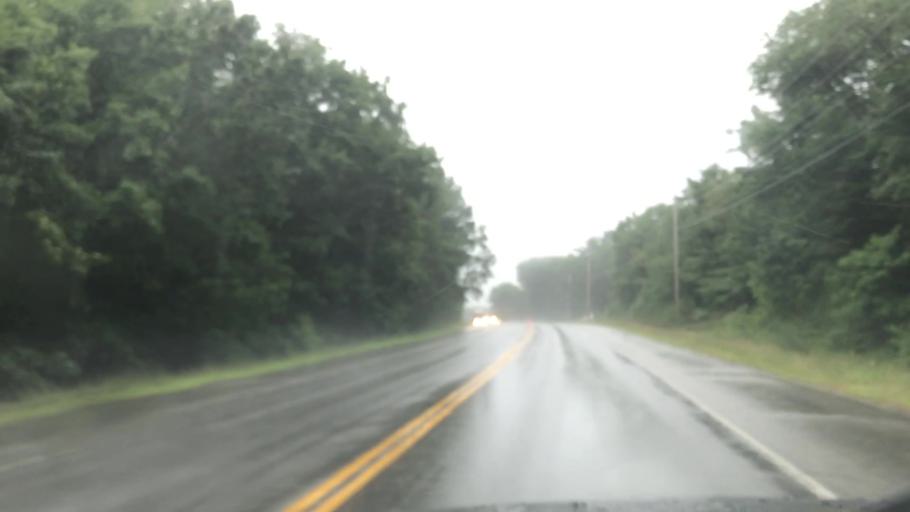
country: US
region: Maine
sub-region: York County
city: Wells Beach Station
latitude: 43.3111
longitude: -70.6549
